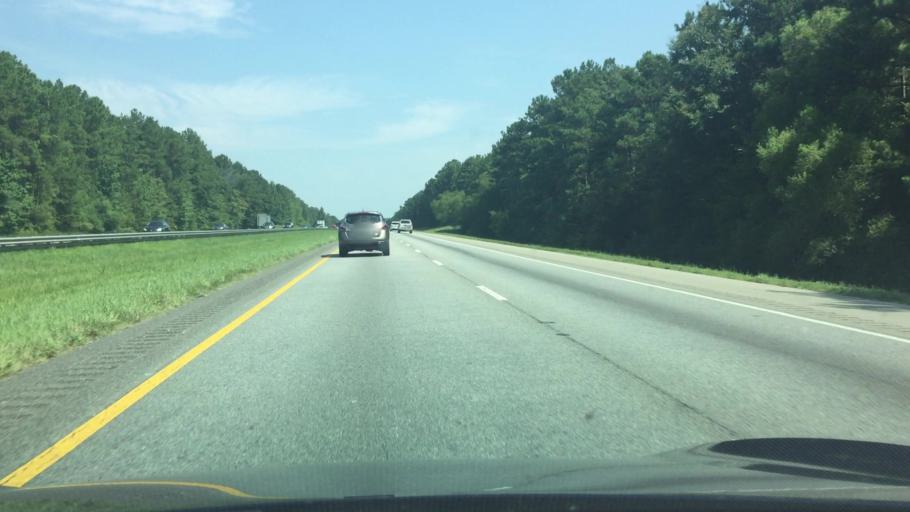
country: US
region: Alabama
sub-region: Shelby County
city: Calera
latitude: 33.1183
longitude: -86.7411
